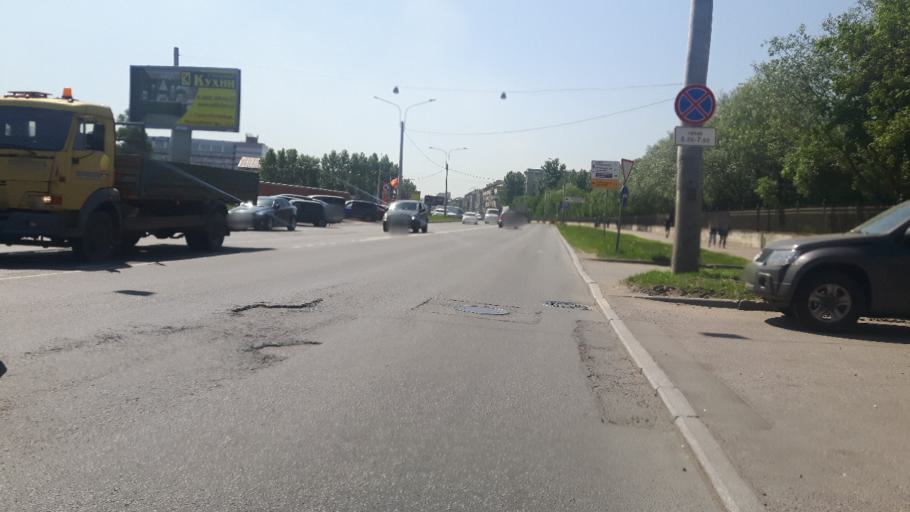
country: RU
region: St.-Petersburg
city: Admiralteisky
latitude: 59.8927
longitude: 30.2814
